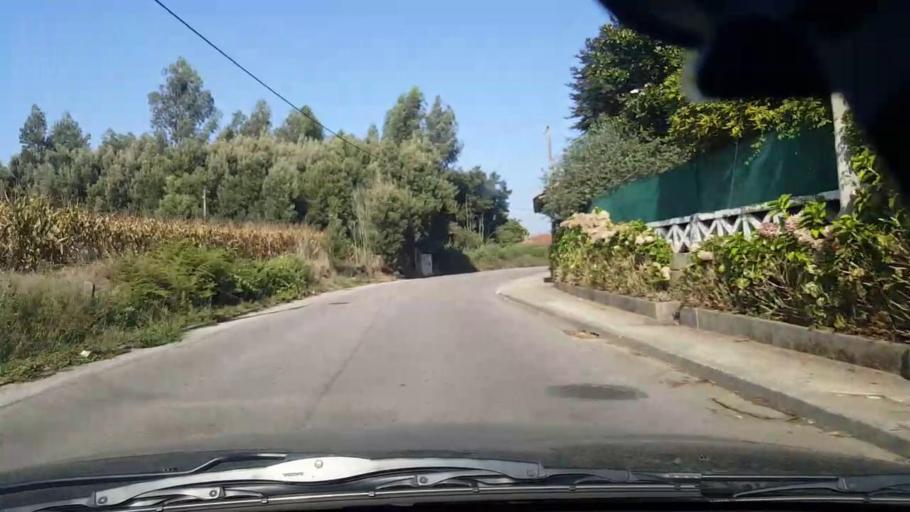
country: PT
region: Porto
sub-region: Maia
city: Gemunde
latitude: 41.2739
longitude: -8.6774
